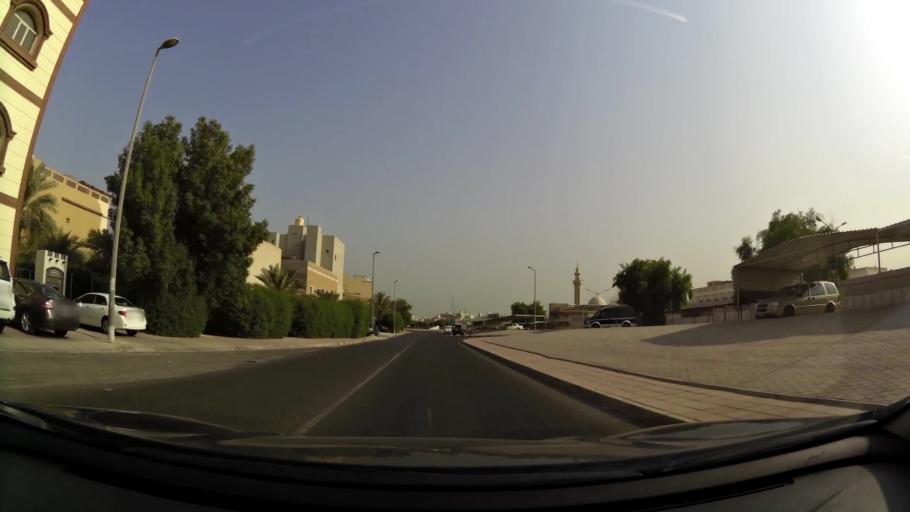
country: KW
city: Al Funaytis
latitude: 29.2168
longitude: 48.0799
